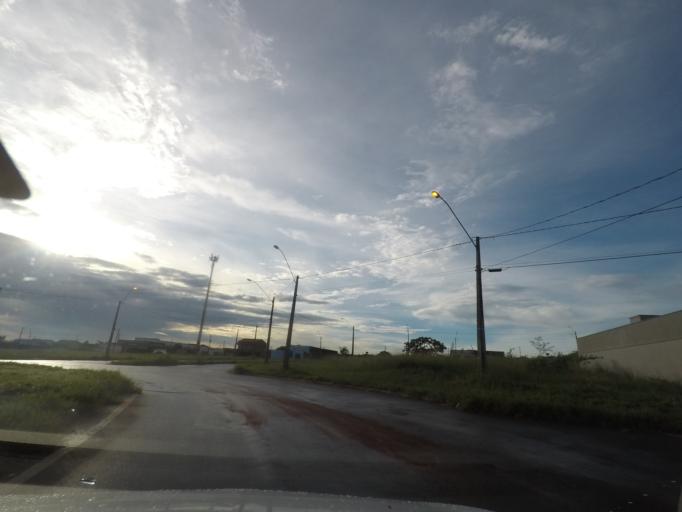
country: BR
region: Goias
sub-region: Goiania
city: Goiania
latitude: -16.7519
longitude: -49.3777
